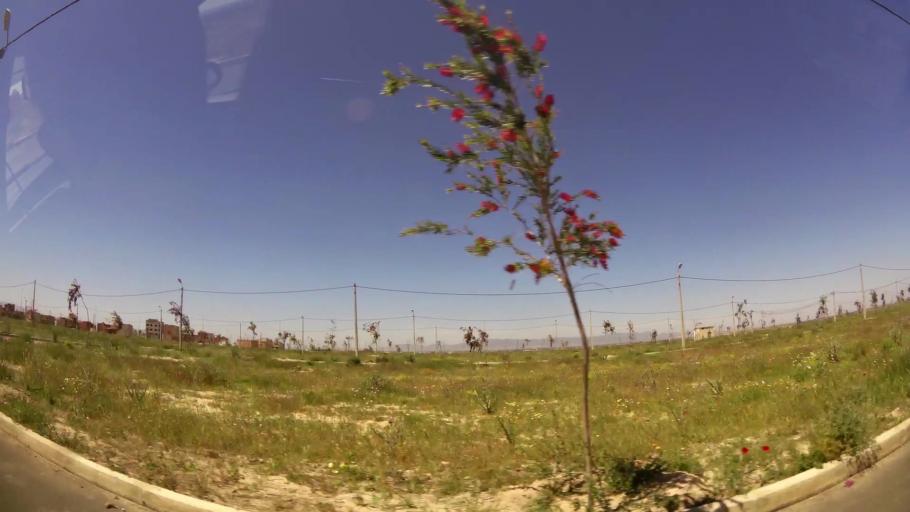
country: MA
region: Oriental
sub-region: Oujda-Angad
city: Oujda
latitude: 34.6829
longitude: -1.8612
